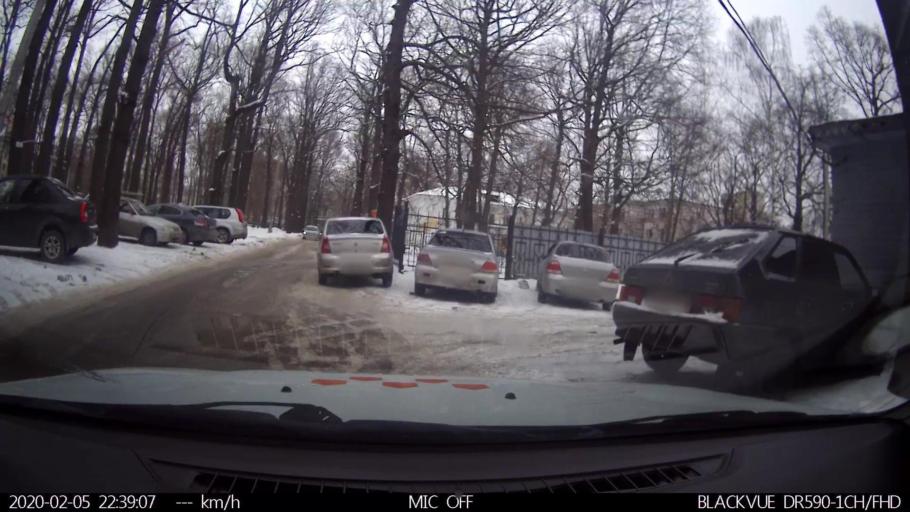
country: RU
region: Nizjnij Novgorod
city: Imeni Stepana Razina
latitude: 54.7266
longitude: 44.2917
